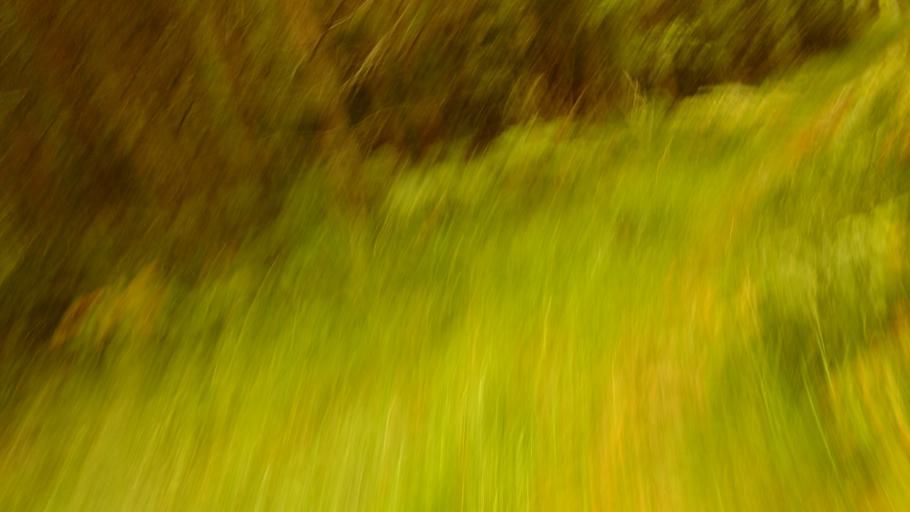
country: FI
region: Varsinais-Suomi
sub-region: Salo
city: Pertteli
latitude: 60.3998
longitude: 23.2190
